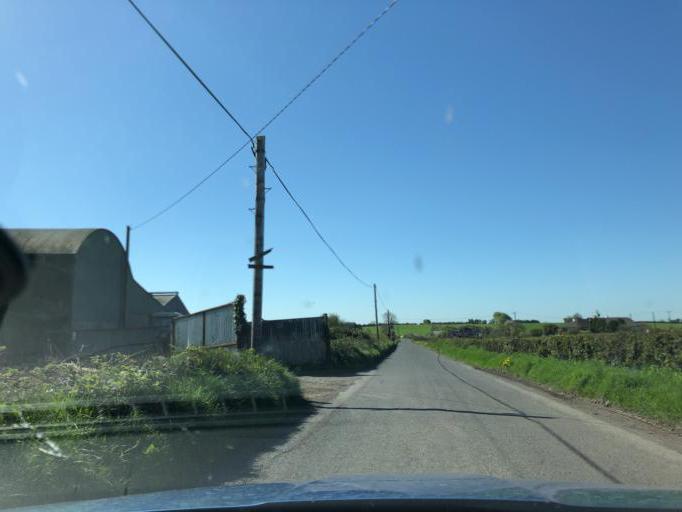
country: IE
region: Connaught
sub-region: County Galway
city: Portumna
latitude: 53.1597
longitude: -8.2949
